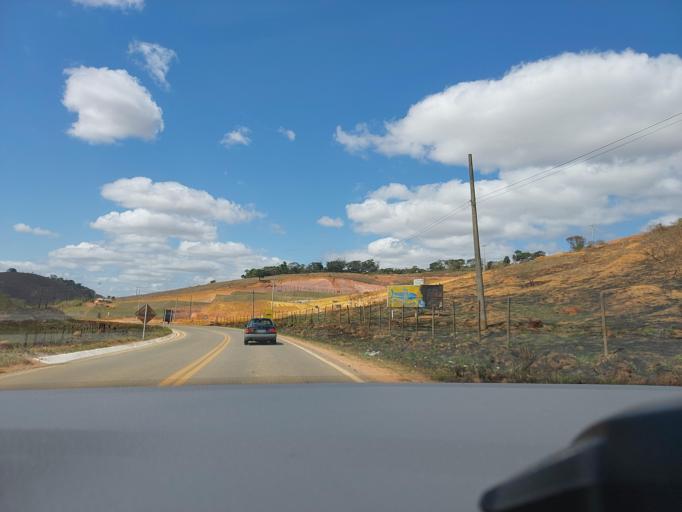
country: BR
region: Minas Gerais
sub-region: Muriae
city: Muriae
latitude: -21.1132
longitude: -42.4419
